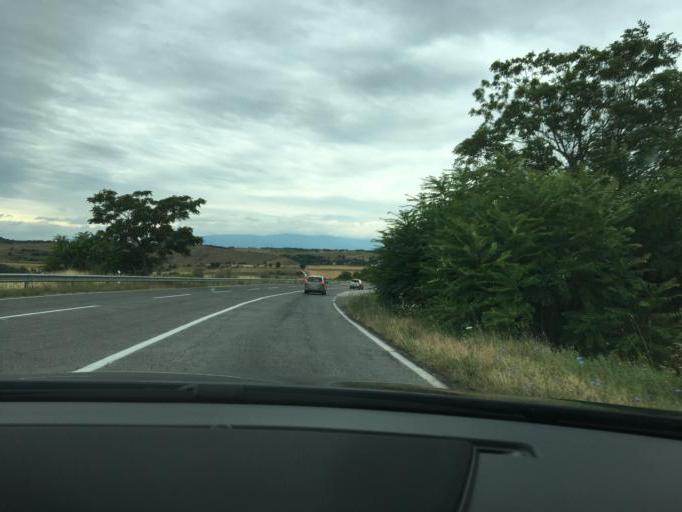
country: MK
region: Staro Nagoricane
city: Staro Nagorichane
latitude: 42.1693
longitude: 21.8107
